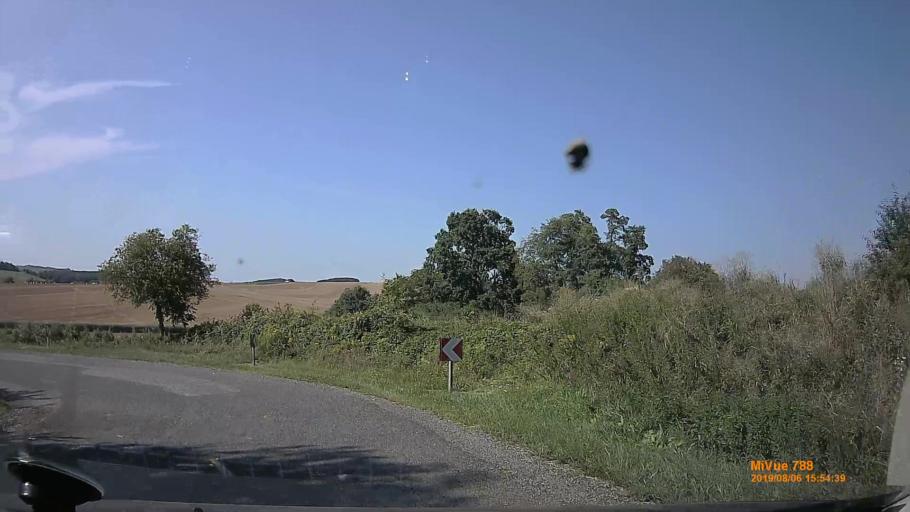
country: HU
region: Somogy
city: Csurgo
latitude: 46.2888
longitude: 17.0250
